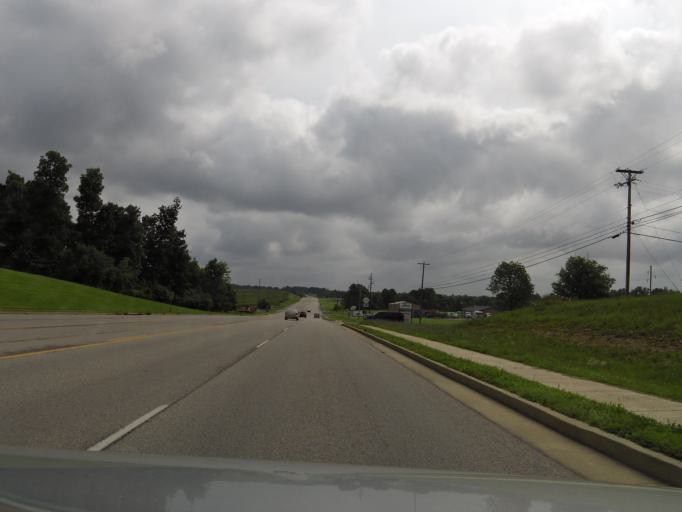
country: US
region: Kentucky
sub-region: Hopkins County
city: Madisonville
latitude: 37.3300
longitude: -87.4337
